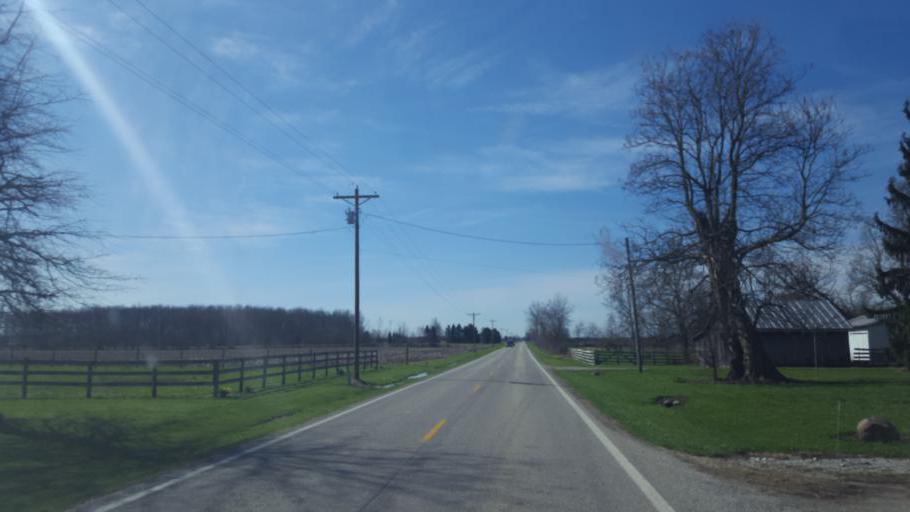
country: US
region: Ohio
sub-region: Morrow County
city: Cardington
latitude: 40.5091
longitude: -82.9629
